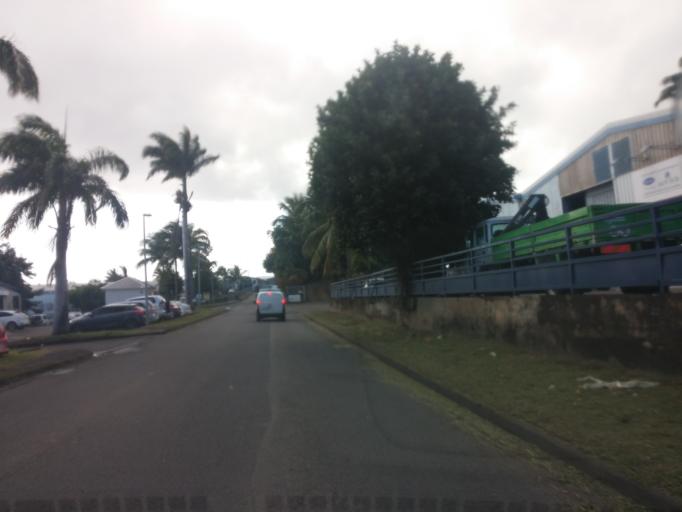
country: RE
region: Reunion
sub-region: Reunion
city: Sainte-Marie
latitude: -20.8998
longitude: 55.5278
